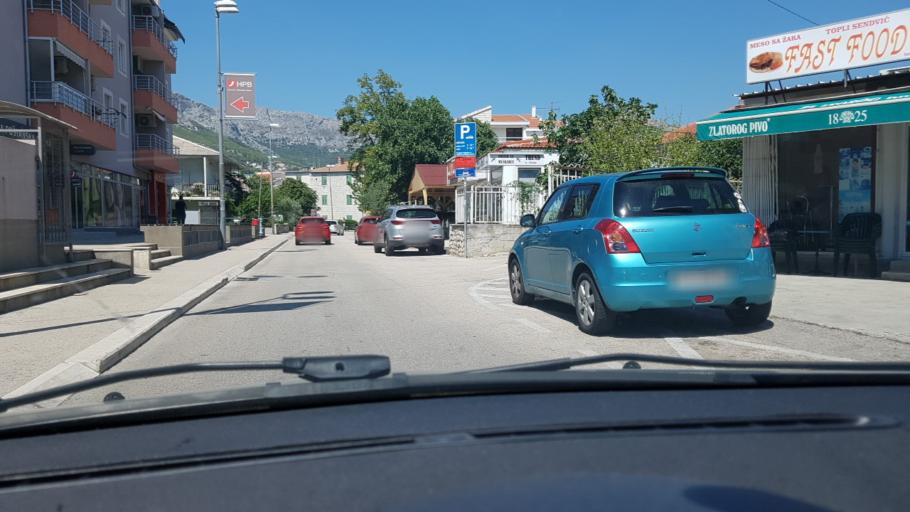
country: HR
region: Splitsko-Dalmatinska
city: Solin
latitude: 43.5365
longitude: 16.4904
